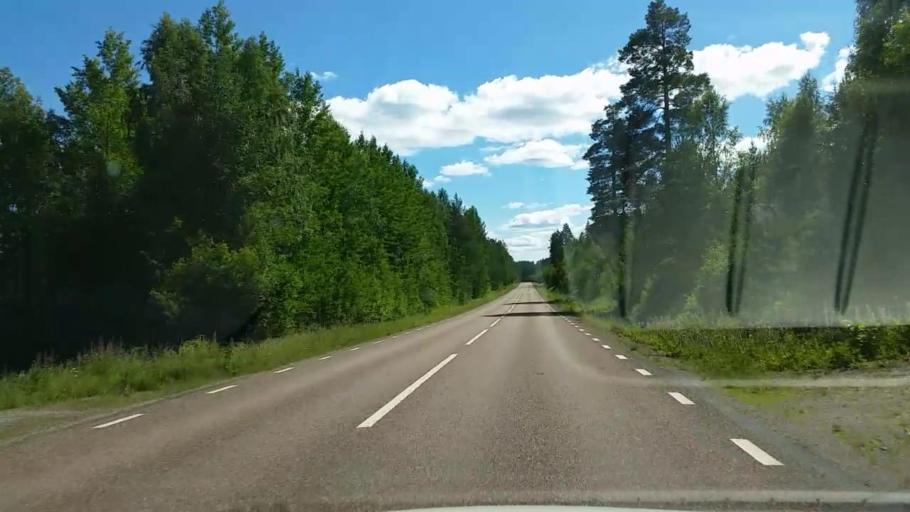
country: SE
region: Dalarna
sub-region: Faluns Kommun
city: Svardsjo
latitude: 60.9686
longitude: 15.6921
